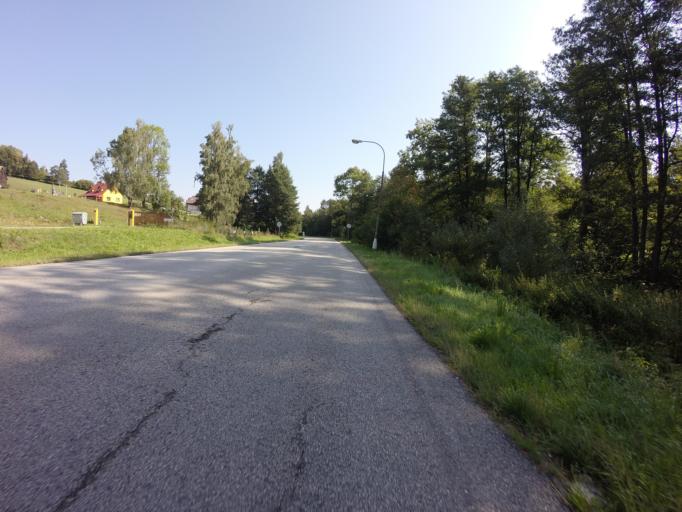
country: CZ
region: Jihocesky
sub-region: Okres Cesky Krumlov
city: Vyssi Brod
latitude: 48.5813
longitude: 14.3195
